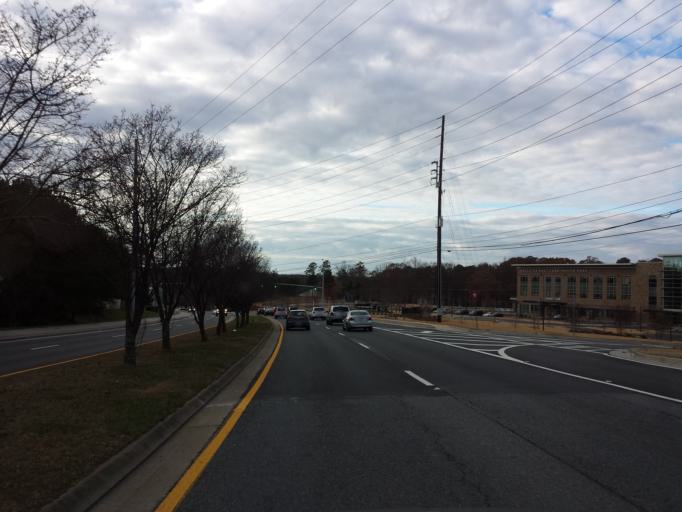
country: US
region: Georgia
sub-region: Fulton County
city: Sandy Springs
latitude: 33.9788
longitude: -84.4431
